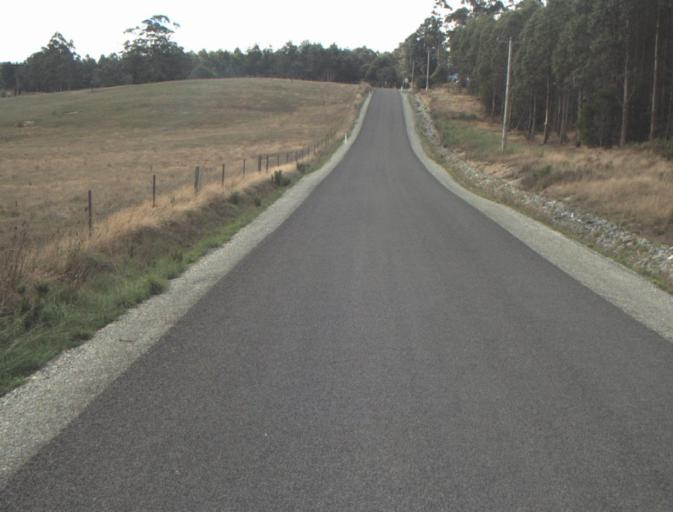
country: AU
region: Tasmania
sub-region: Launceston
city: Mayfield
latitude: -41.1959
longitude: 147.1812
